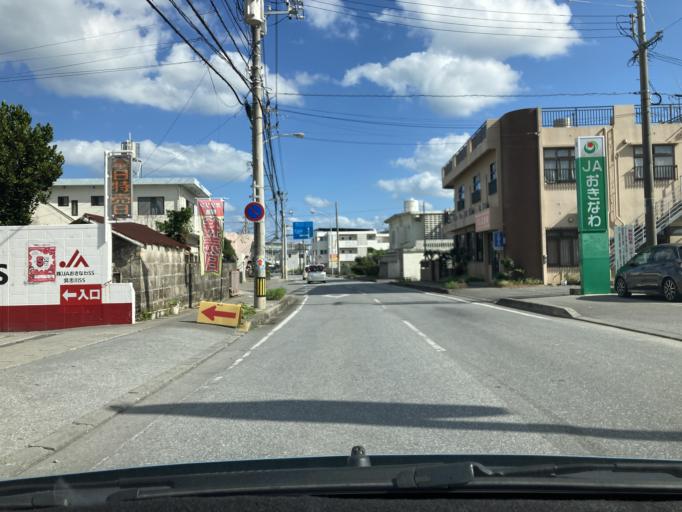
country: JP
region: Okinawa
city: Gushikawa
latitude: 26.3492
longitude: 127.8499
